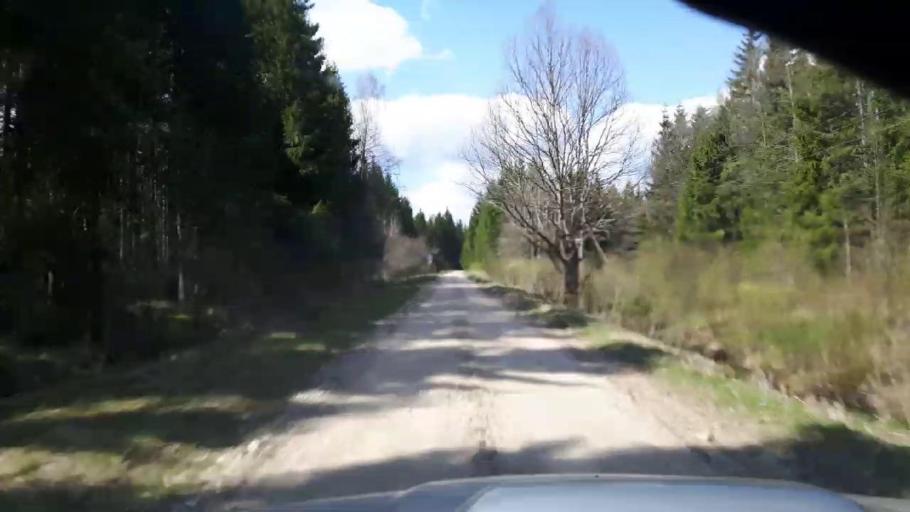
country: EE
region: Paernumaa
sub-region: Tootsi vald
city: Tootsi
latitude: 58.4465
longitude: 24.9060
